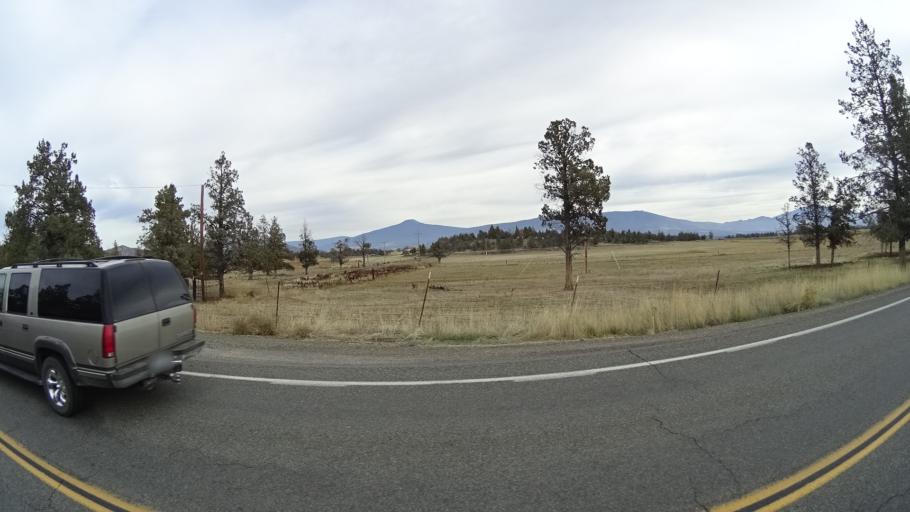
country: US
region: California
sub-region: Siskiyou County
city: Montague
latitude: 41.6322
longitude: -122.4346
